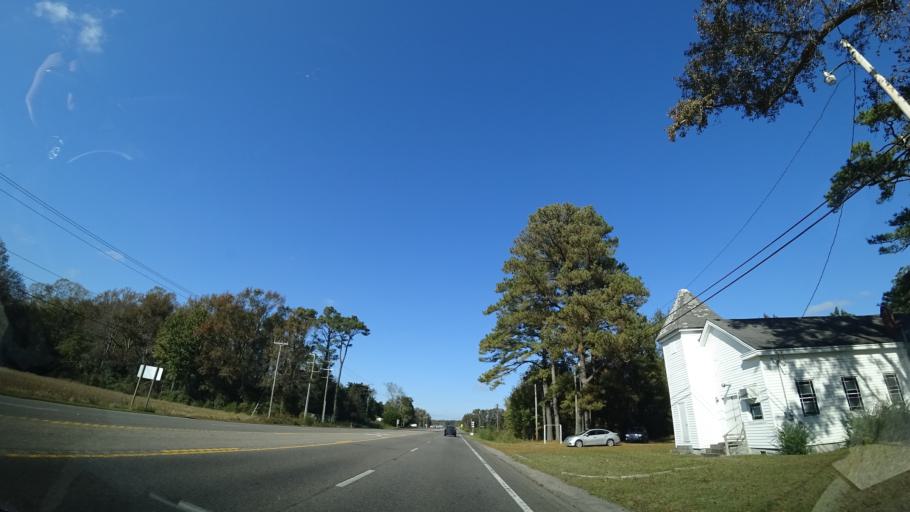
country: US
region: North Carolina
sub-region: Currituck County
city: Currituck
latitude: 36.2727
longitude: -75.9106
